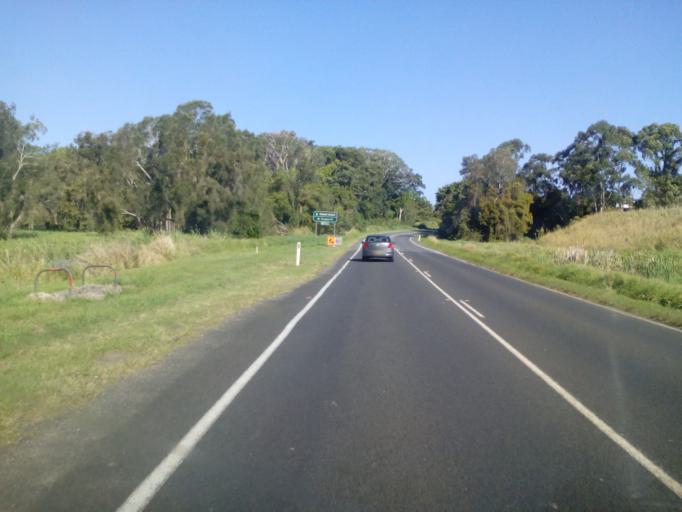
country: AU
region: New South Wales
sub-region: Tweed
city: Kingscliff
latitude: -28.2601
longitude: 153.5611
